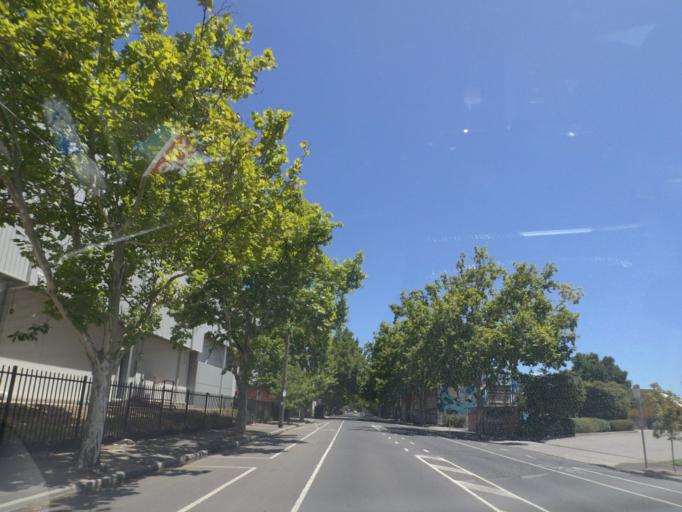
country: AU
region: Victoria
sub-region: Moonee Valley
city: Flemington
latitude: -37.7993
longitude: 144.9187
